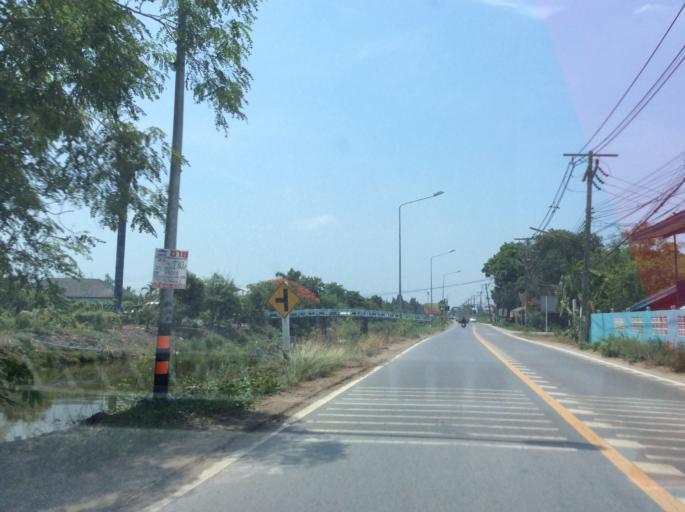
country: TH
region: Pathum Thani
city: Ban Rangsit
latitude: 14.0206
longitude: 100.7783
